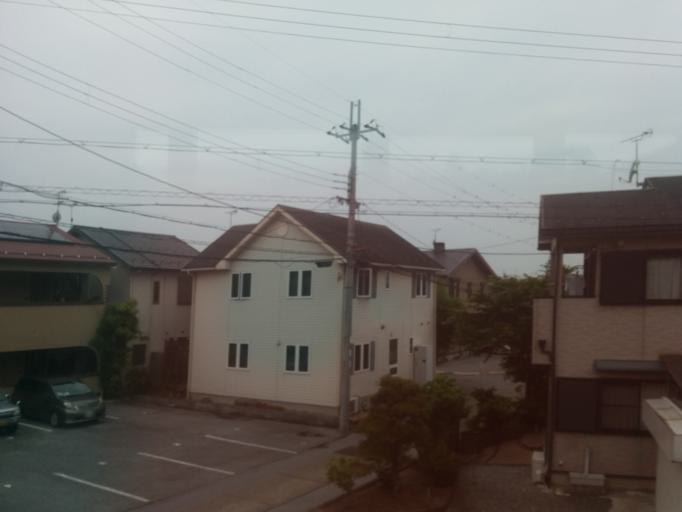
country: JP
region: Shiga Prefecture
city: Hikone
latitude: 35.2823
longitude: 136.2645
